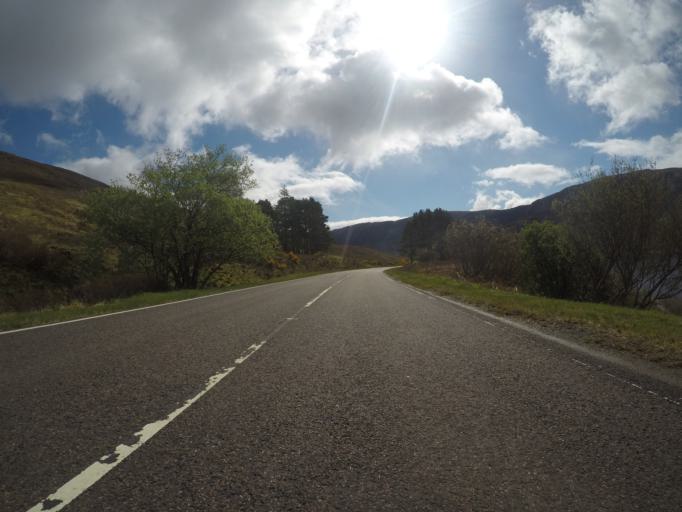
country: GB
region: Scotland
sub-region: Highland
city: Spean Bridge
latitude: 57.1464
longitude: -5.0929
